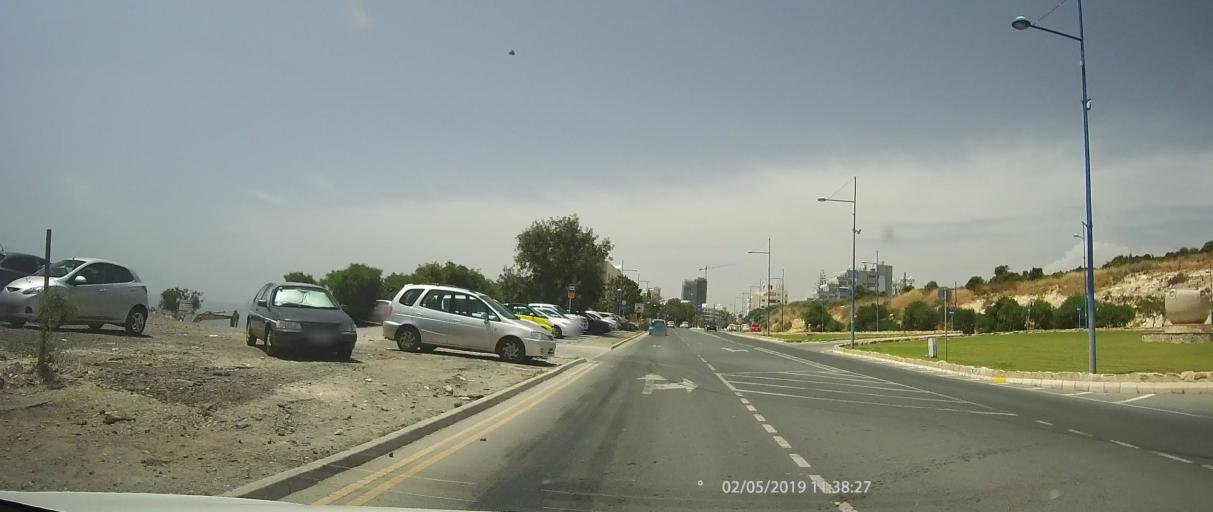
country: CY
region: Larnaka
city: Agios Tychon
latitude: 34.7096
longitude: 33.1372
